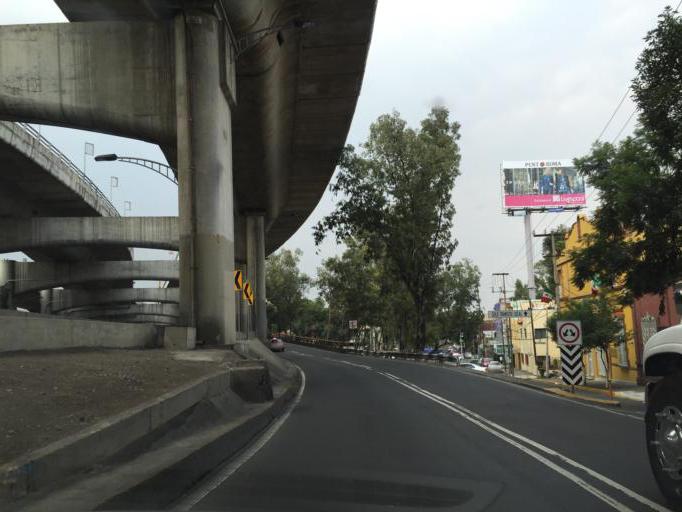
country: MX
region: Mexico City
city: Alvaro Obregon
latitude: 19.3716
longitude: -99.1914
